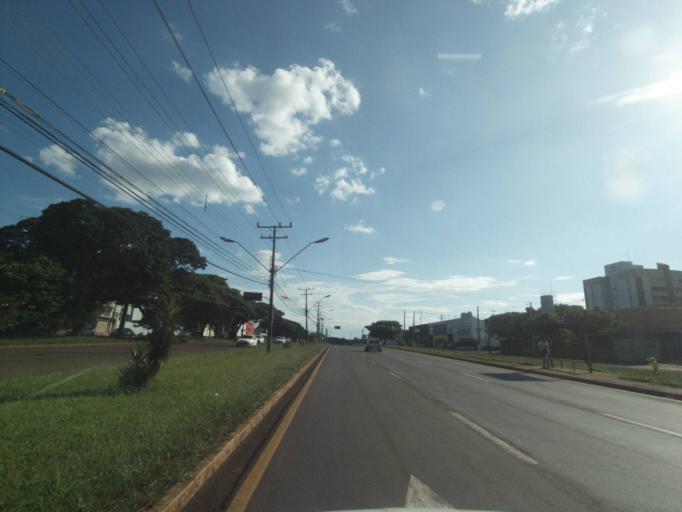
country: BR
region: Parana
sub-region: Londrina
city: Londrina
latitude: -23.3518
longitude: -51.1475
